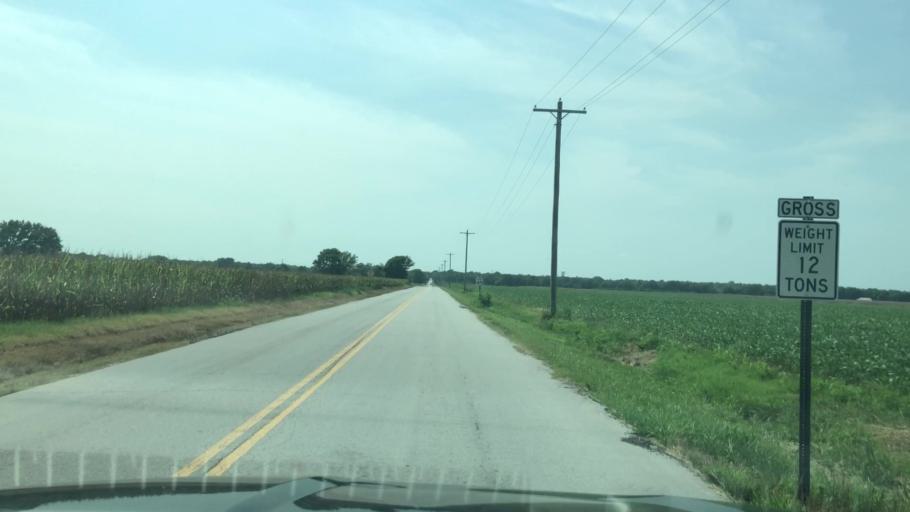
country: US
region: Oklahoma
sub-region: Ottawa County
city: Commerce
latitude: 36.9292
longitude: -94.8425
